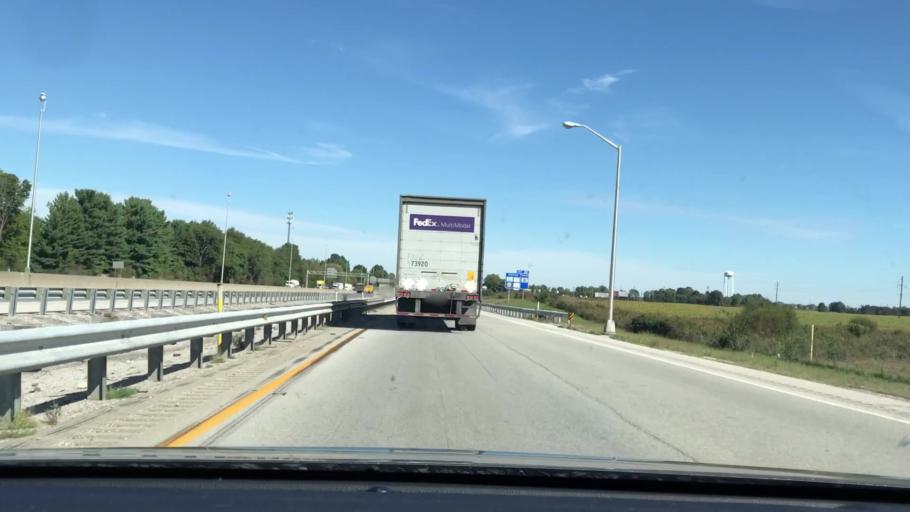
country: US
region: Kentucky
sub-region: Warren County
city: Plano
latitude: 36.9146
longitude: -86.4294
